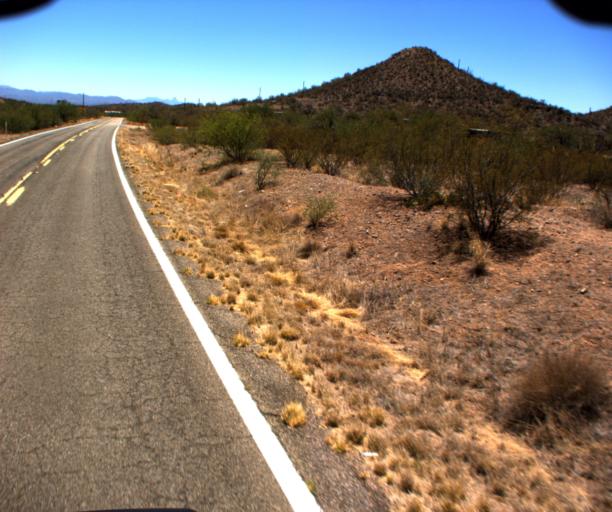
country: US
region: Arizona
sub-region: Pima County
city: Sells
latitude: 32.1740
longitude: -112.1554
